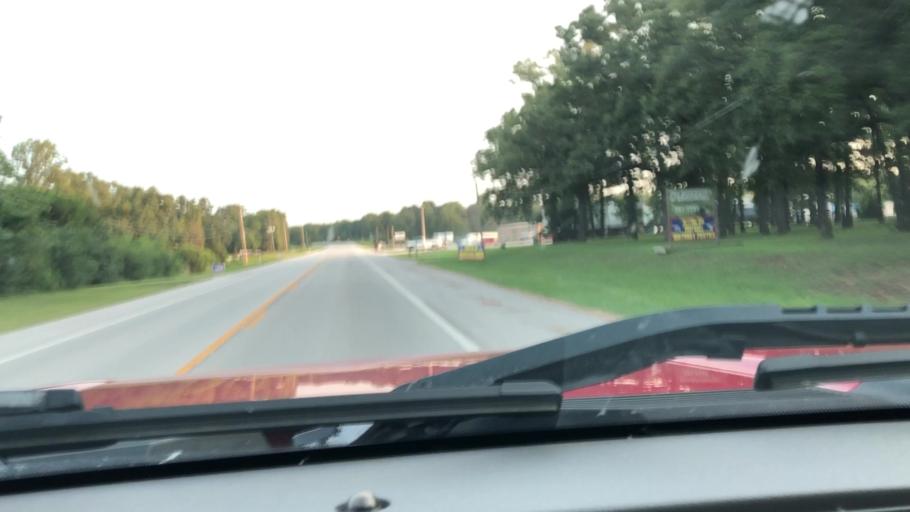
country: US
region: Missouri
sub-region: Jasper County
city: Duquesne
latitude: 36.9849
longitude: -94.4638
